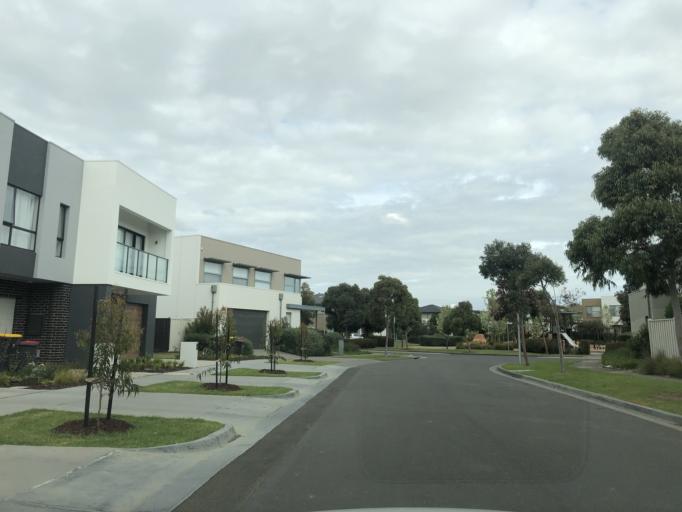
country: AU
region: Victoria
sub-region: Monash
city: Mulgrave
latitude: -37.9311
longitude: 145.1922
